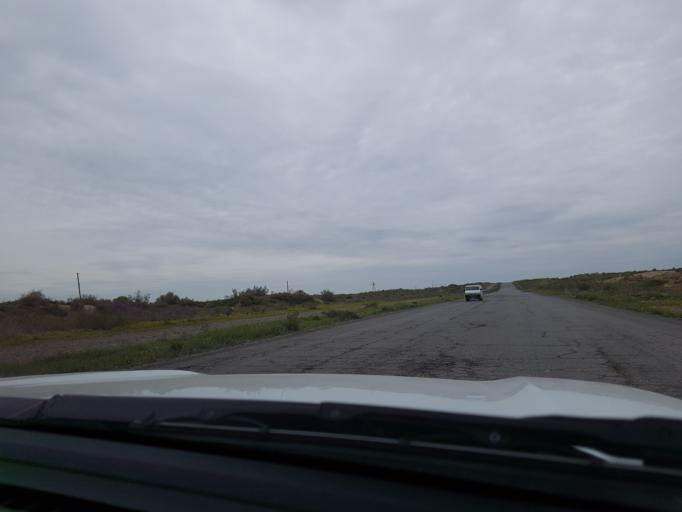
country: TM
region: Mary
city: Bayramaly
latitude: 37.8910
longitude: 62.6154
